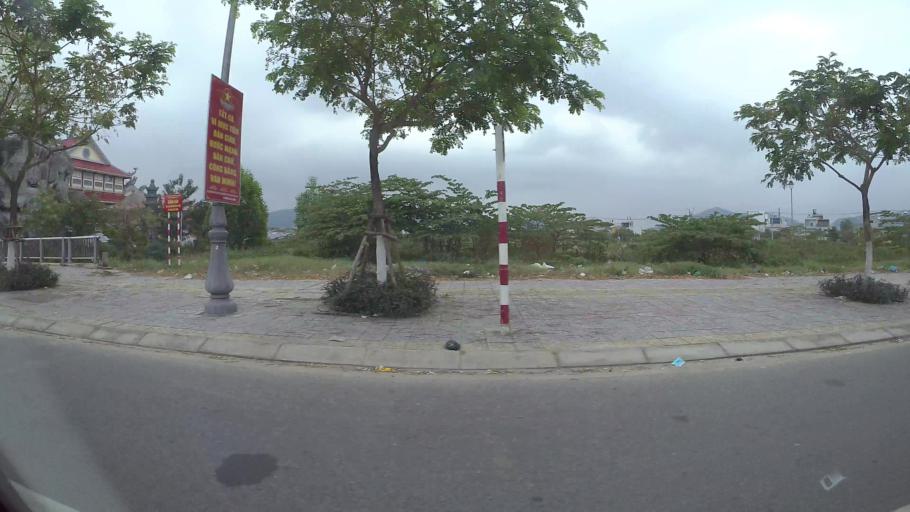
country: VN
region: Da Nang
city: Lien Chieu
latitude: 16.0662
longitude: 108.1722
